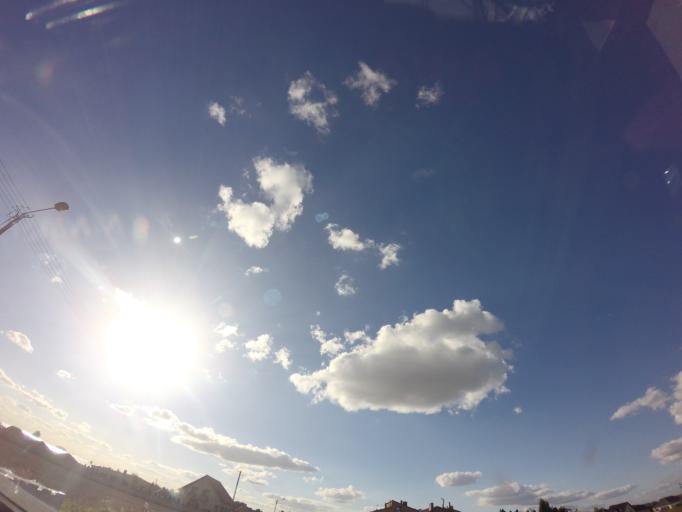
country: PL
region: Greater Poland Voivodeship
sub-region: Powiat koscianski
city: Smigiel
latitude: 52.0620
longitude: 16.4462
